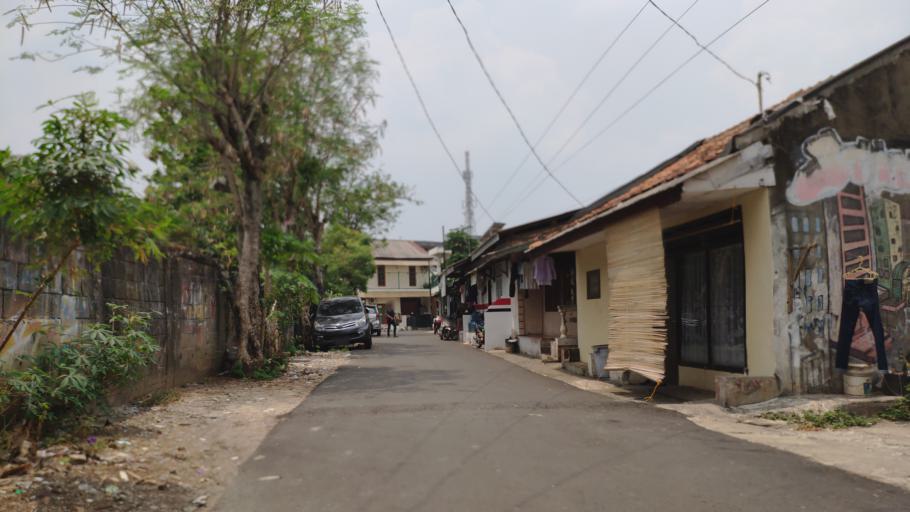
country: ID
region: Banten
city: South Tangerang
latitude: -6.2682
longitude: 106.7771
